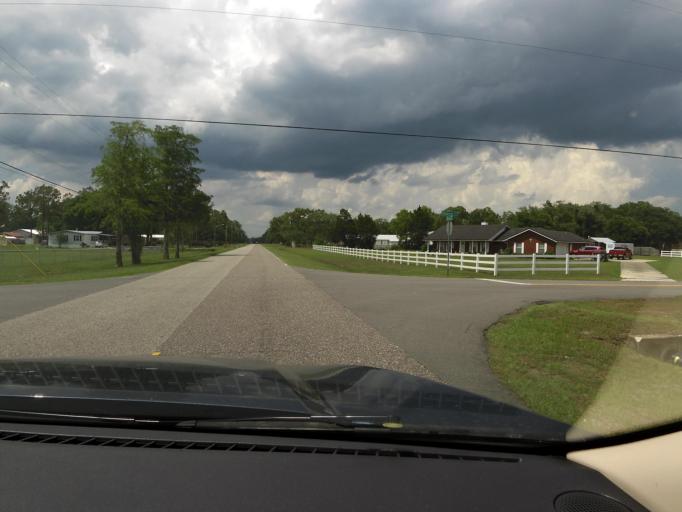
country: US
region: Florida
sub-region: Duval County
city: Baldwin
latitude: 30.3206
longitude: -81.8694
